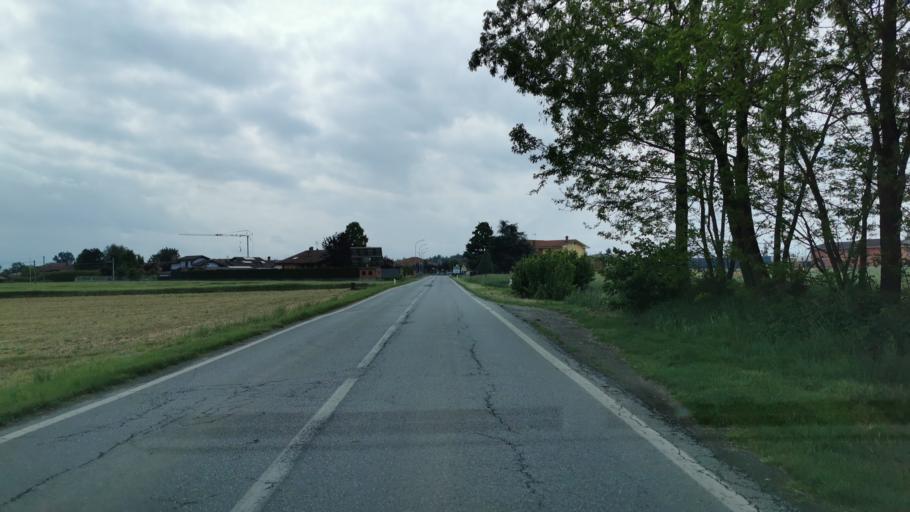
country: IT
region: Piedmont
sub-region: Provincia di Cuneo
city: Villafalletto
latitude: 44.5551
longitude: 7.5366
